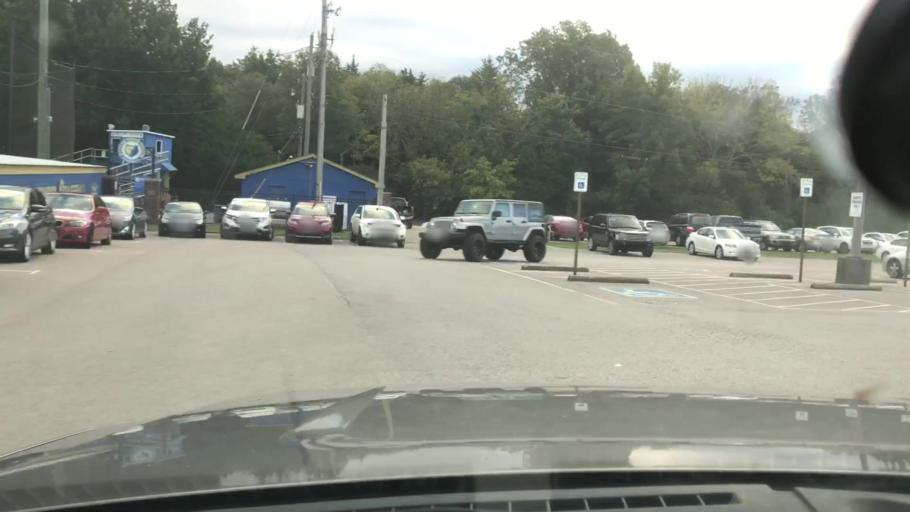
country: US
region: Tennessee
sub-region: Williamson County
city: Brentwood
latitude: 36.0169
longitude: -86.8142
